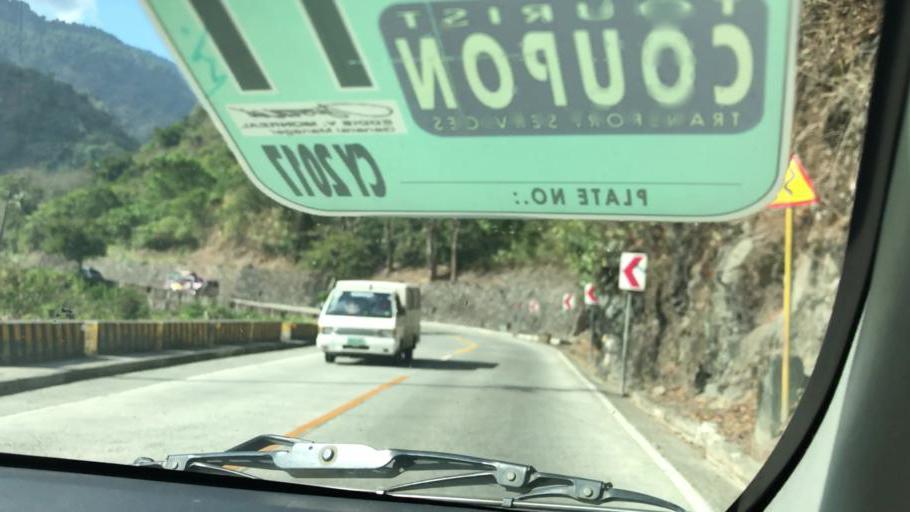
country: PH
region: Cordillera
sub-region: Province of Benguet
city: Tuba
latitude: 16.3166
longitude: 120.6183
